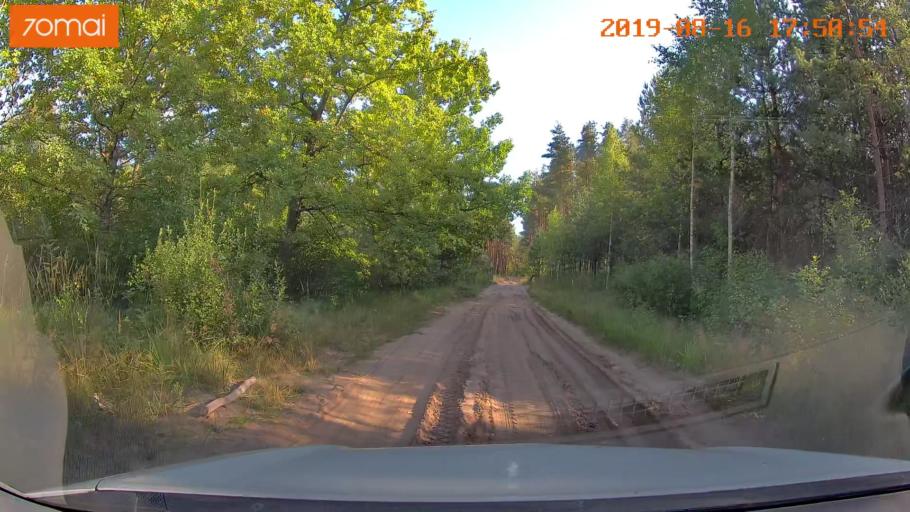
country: BY
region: Mogilev
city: Asipovichy
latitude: 53.2262
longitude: 28.6589
